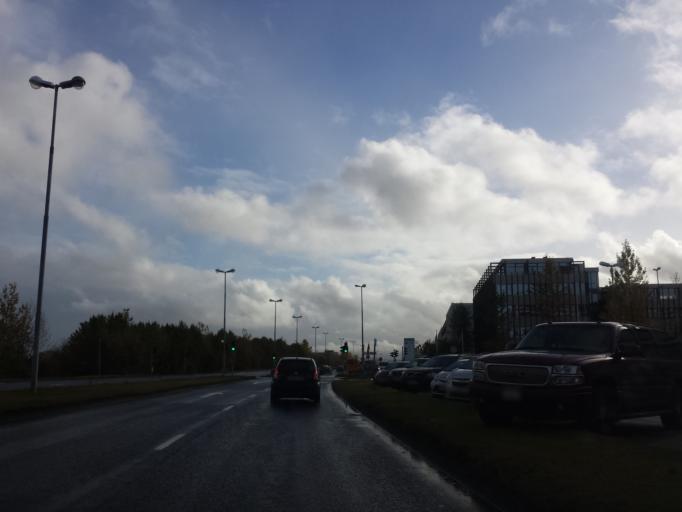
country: IS
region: Capital Region
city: Reykjavik
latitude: 64.1397
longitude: -21.8817
